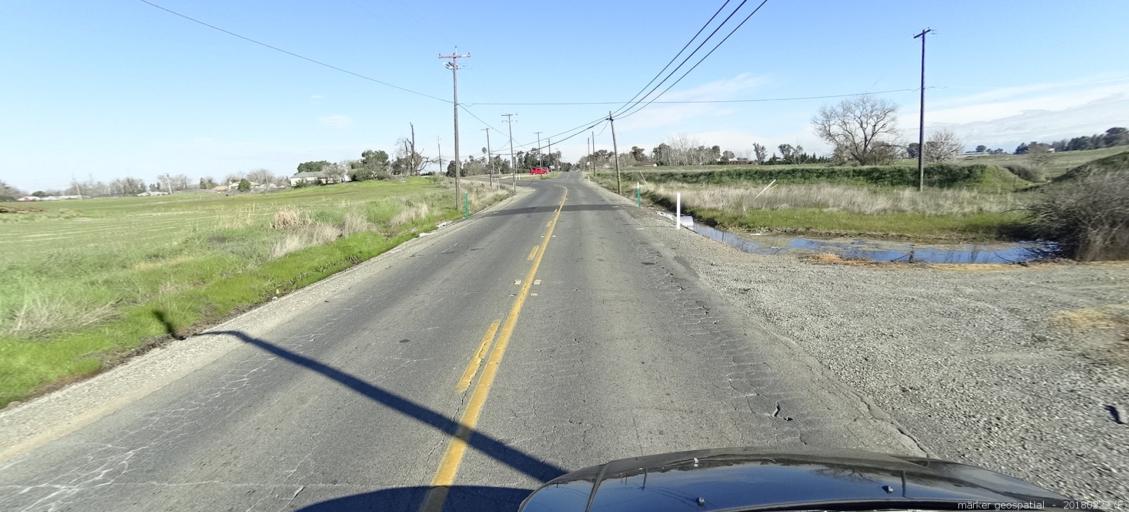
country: US
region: California
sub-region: Sacramento County
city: Elverta
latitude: 38.7199
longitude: -121.4666
